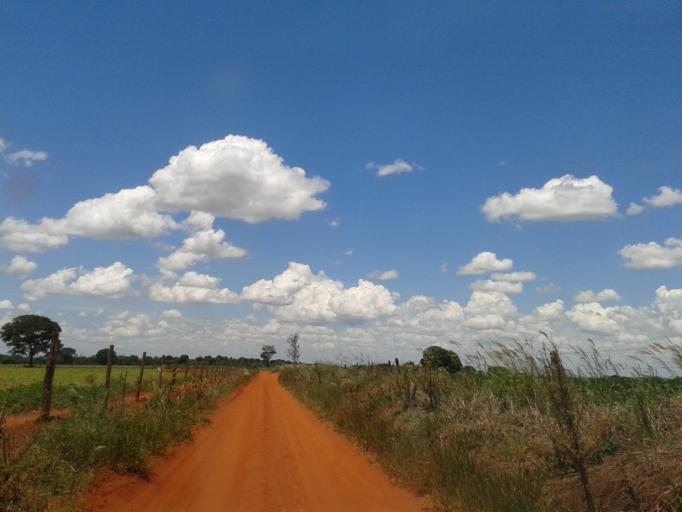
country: BR
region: Minas Gerais
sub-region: Centralina
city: Centralina
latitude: -18.6963
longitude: -49.1663
